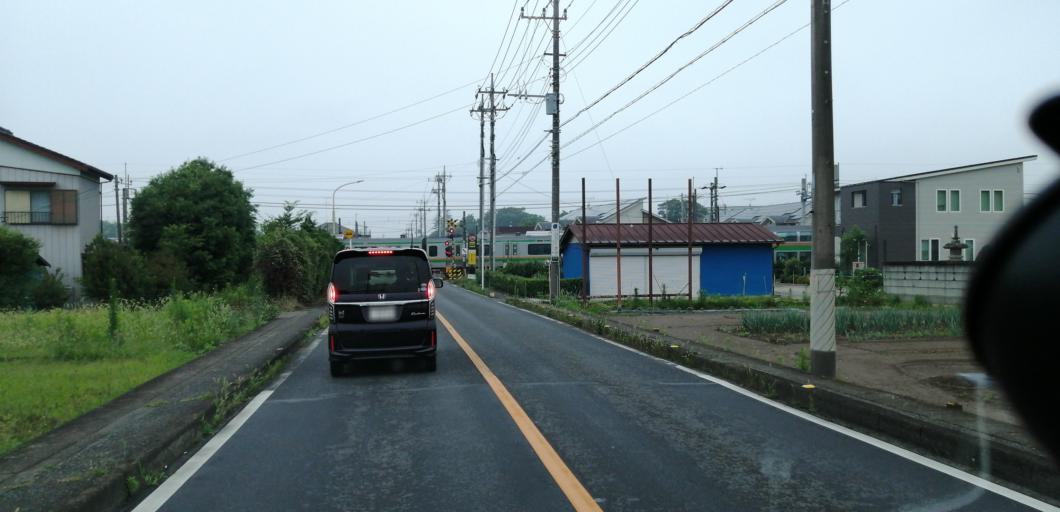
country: JP
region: Saitama
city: Kukichuo
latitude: 36.1000
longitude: 139.6795
